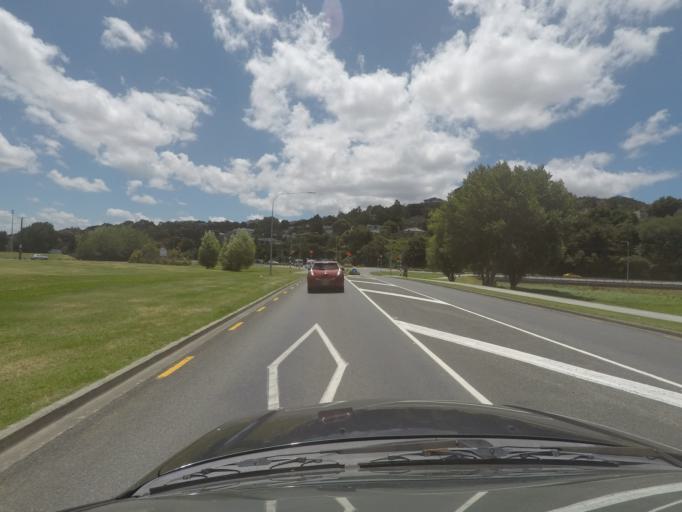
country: NZ
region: Northland
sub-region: Whangarei
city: Whangarei
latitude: -35.7321
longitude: 174.3428
